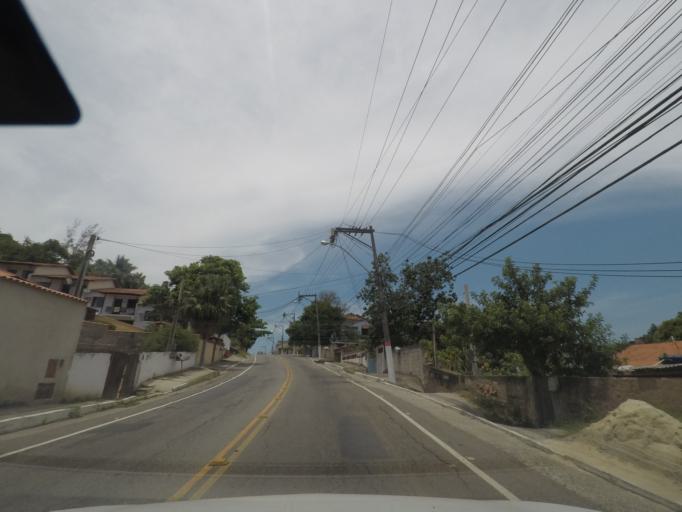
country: BR
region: Rio de Janeiro
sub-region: Marica
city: Marica
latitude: -22.9264
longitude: -42.8200
